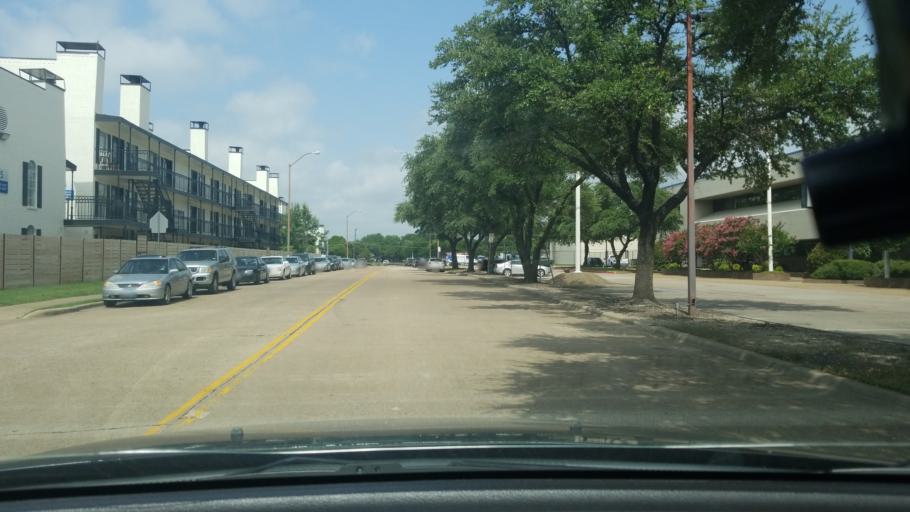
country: US
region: Texas
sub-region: Dallas County
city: Mesquite
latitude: 32.8028
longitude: -96.6889
